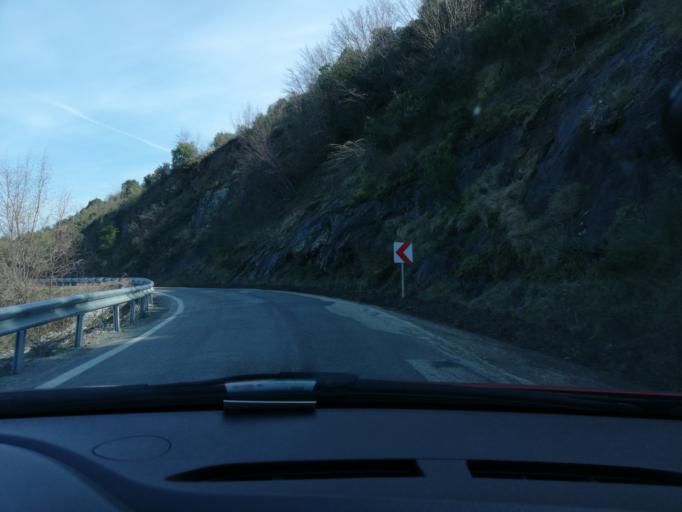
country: TR
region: Bartin
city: Kurucasile
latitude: 41.8278
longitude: 32.6396
